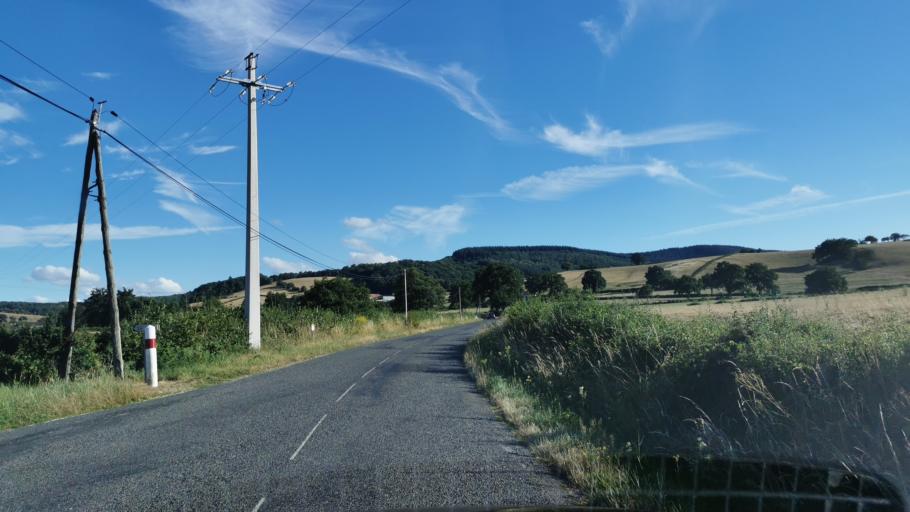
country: FR
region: Bourgogne
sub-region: Departement de Saone-et-Loire
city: Marmagne
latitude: 46.8087
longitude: 4.3286
